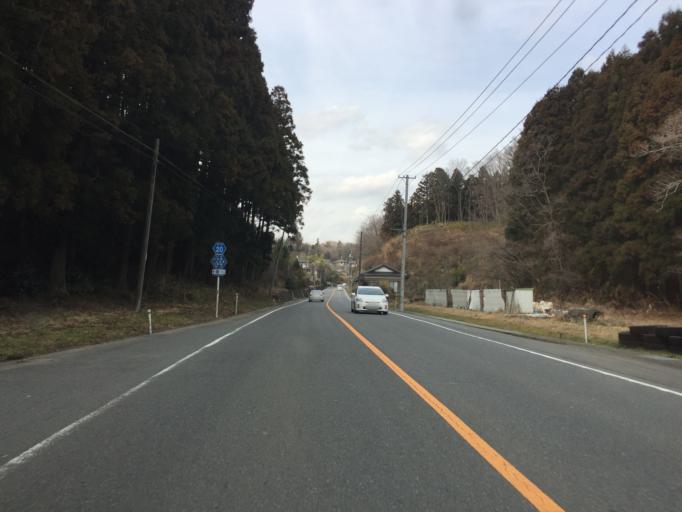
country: JP
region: Fukushima
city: Iwaki
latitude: 36.9734
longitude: 140.7397
